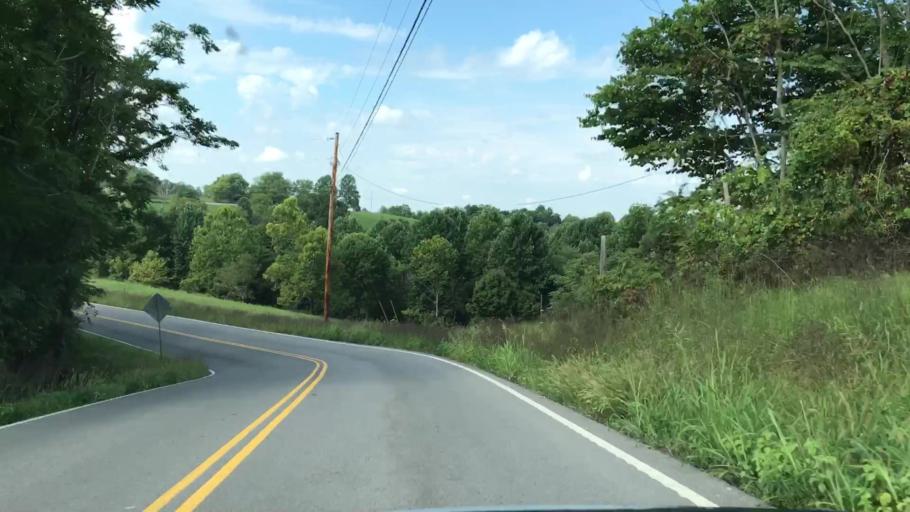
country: US
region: Tennessee
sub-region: Sumner County
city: Westmoreland
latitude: 36.5080
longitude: -86.1856
